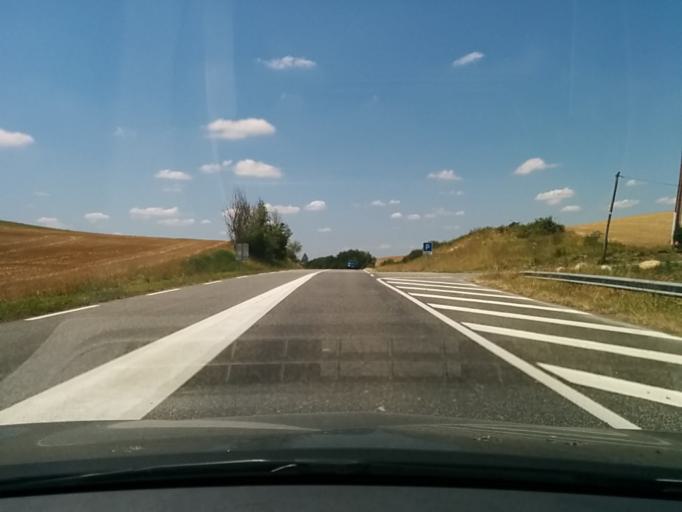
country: FR
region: Midi-Pyrenees
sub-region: Departement du Gers
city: Jegun
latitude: 43.7141
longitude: 0.4273
